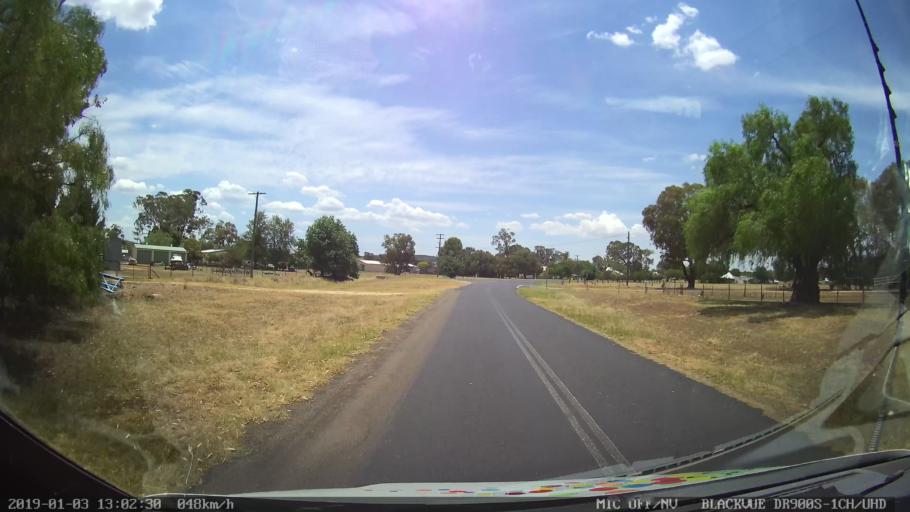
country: AU
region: New South Wales
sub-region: Cabonne
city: Canowindra
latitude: -33.6177
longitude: 148.4294
